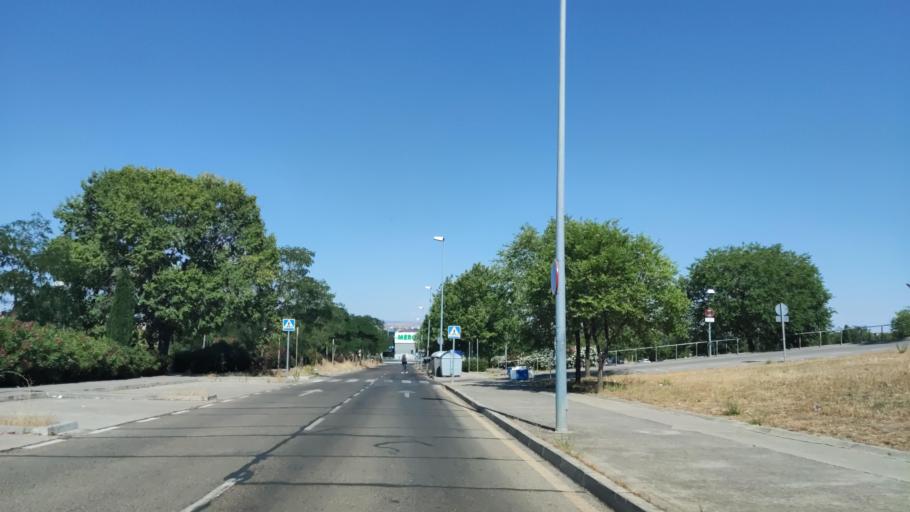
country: ES
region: Madrid
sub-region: Provincia de Madrid
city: Leganes
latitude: 40.3414
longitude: -3.7603
